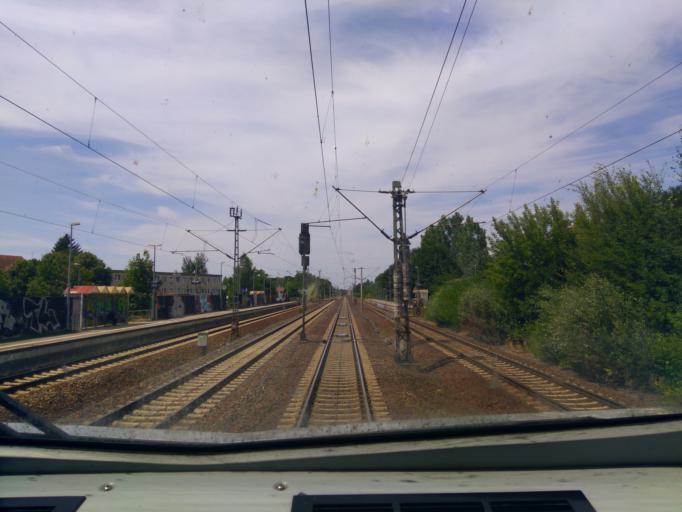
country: DE
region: Brandenburg
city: Brieselang
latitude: 52.5822
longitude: 13.0029
